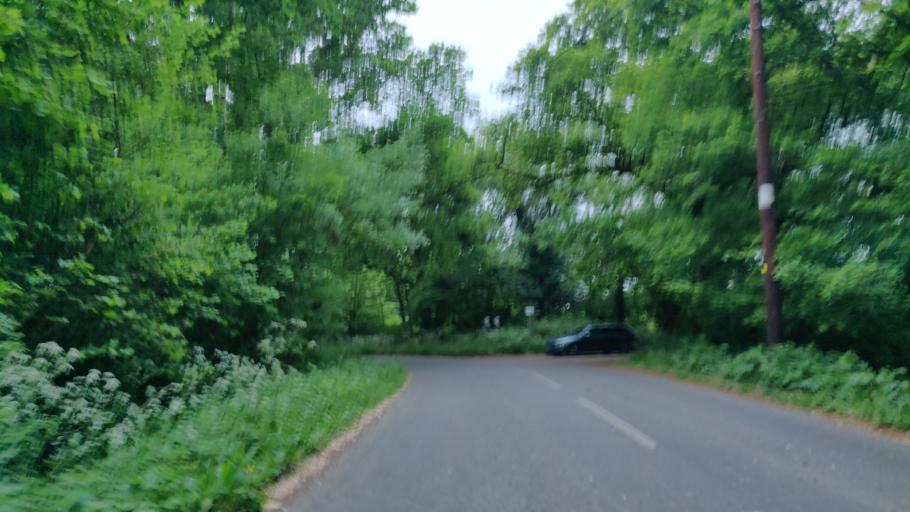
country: GB
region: England
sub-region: West Sussex
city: Southwater
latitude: 51.0391
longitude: -0.3373
